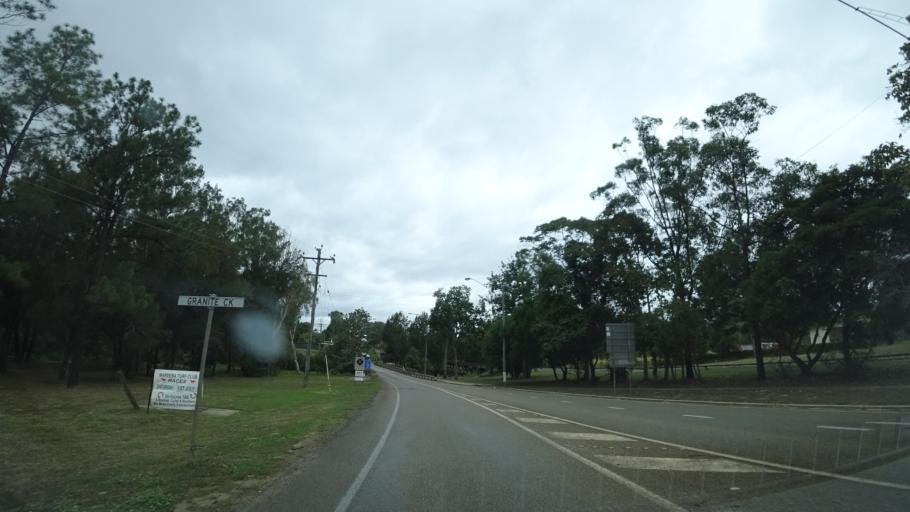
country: AU
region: Queensland
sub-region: Tablelands
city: Mareeba
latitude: -16.9854
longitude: 145.4187
